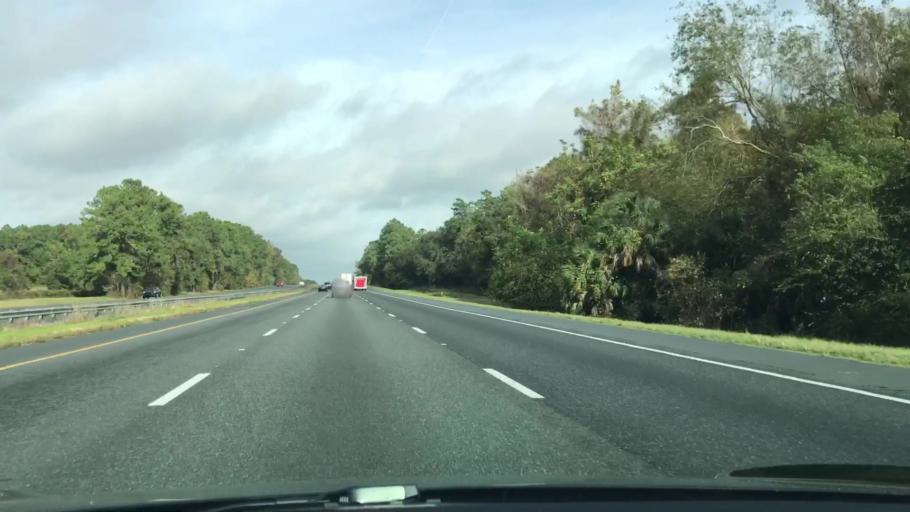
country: US
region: Florida
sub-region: Marion County
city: Citra
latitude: 29.3706
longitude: -82.2281
